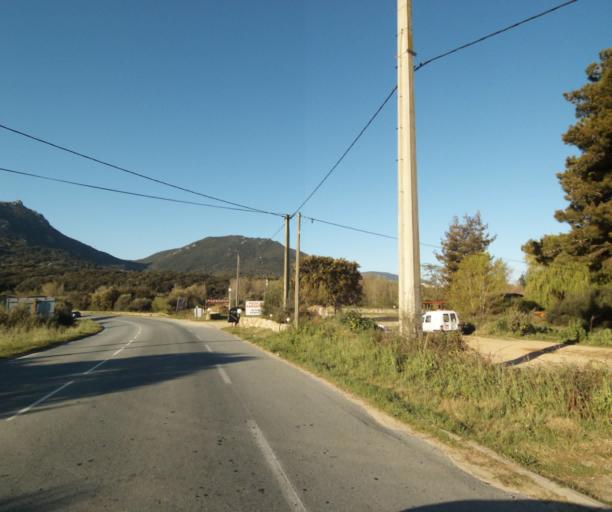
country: FR
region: Corsica
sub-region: Departement de la Corse-du-Sud
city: Propriano
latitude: 41.6611
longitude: 8.9173
